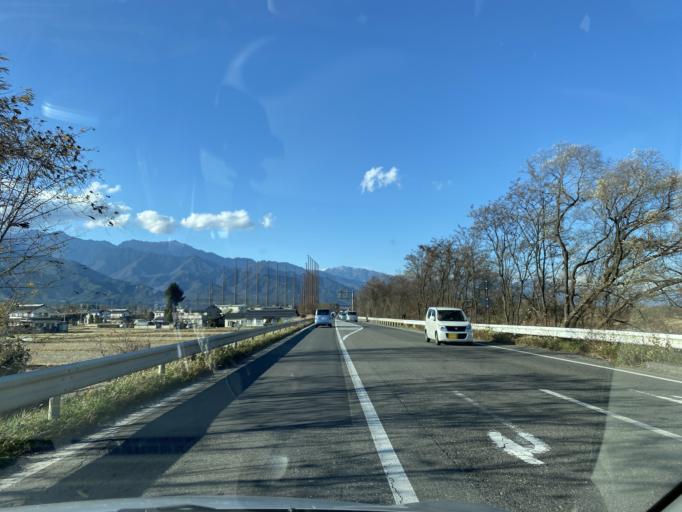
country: JP
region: Nagano
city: Hotaka
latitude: 36.3753
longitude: 137.8754
